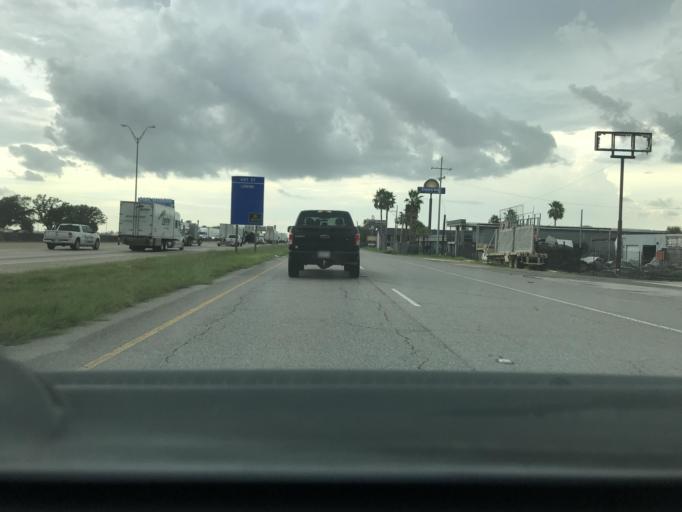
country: US
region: Louisiana
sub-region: Calcasieu Parish
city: Westlake
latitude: 30.2374
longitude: -93.2287
